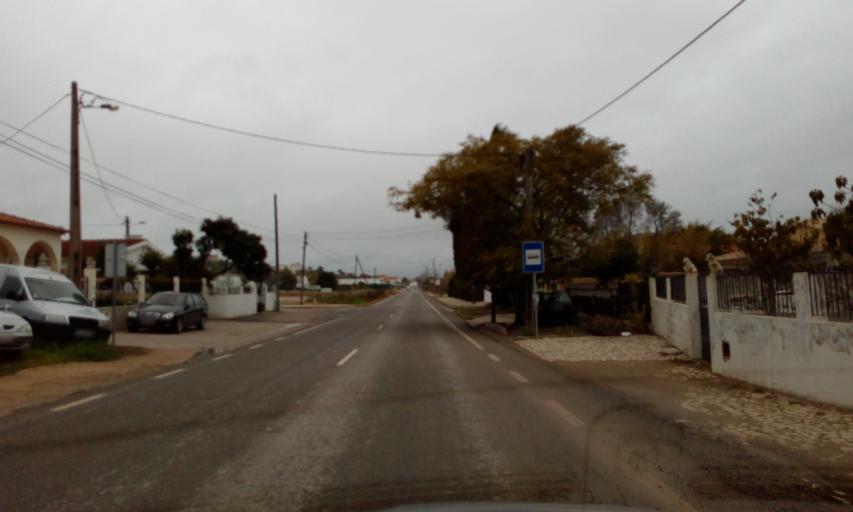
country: PT
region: Faro
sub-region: Albufeira
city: Guia
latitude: 37.1578
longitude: -8.2909
